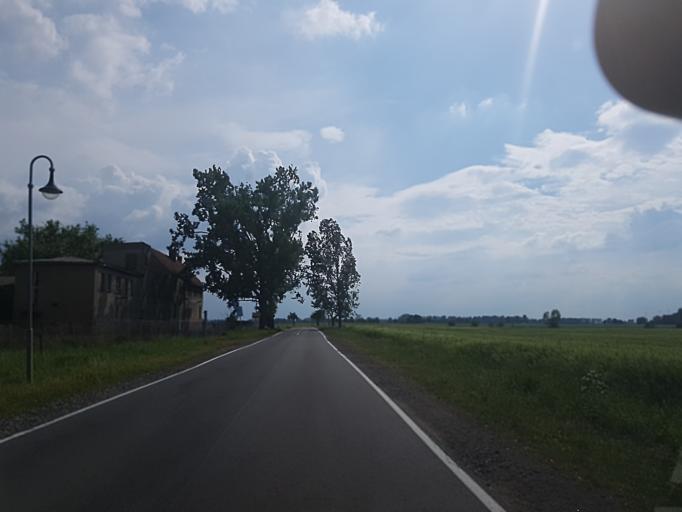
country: DE
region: Saxony-Anhalt
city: Lindau
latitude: 52.0222
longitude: 12.2249
